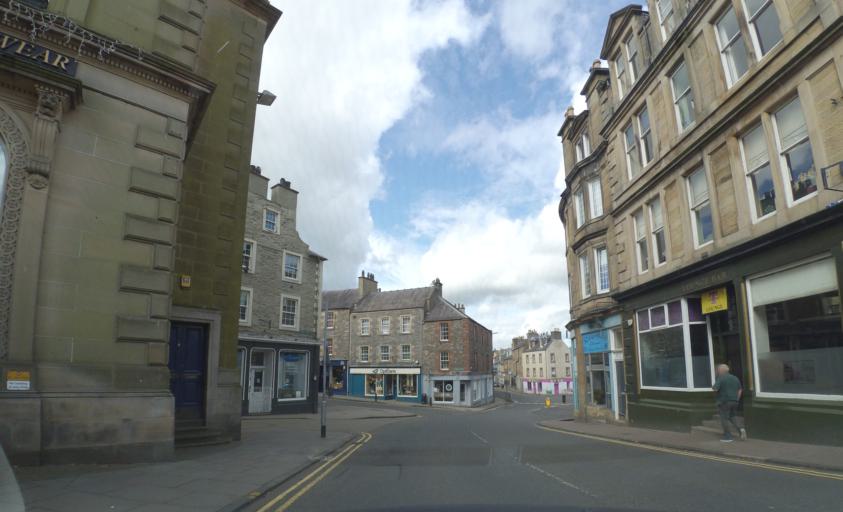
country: GB
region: Scotland
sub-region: The Scottish Borders
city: Hawick
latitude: 55.4213
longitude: -2.7886
